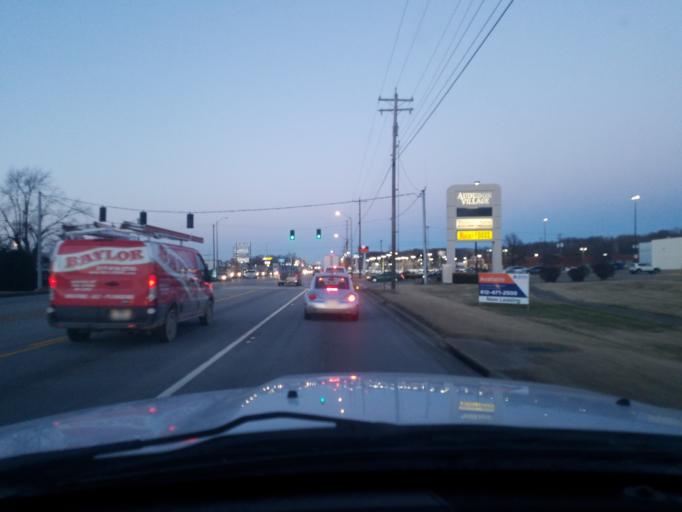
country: US
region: Kentucky
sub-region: Henderson County
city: Henderson
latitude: 37.8710
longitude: -87.5701
